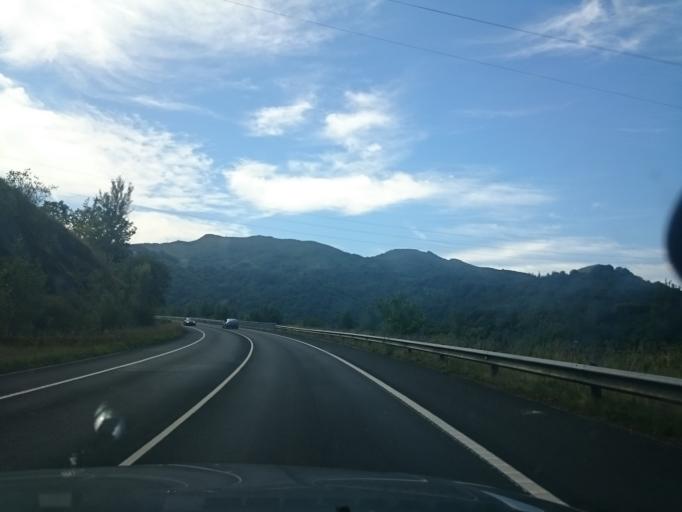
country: ES
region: Asturias
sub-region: Province of Asturias
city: Oviedo
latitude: 43.3057
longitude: -5.8303
